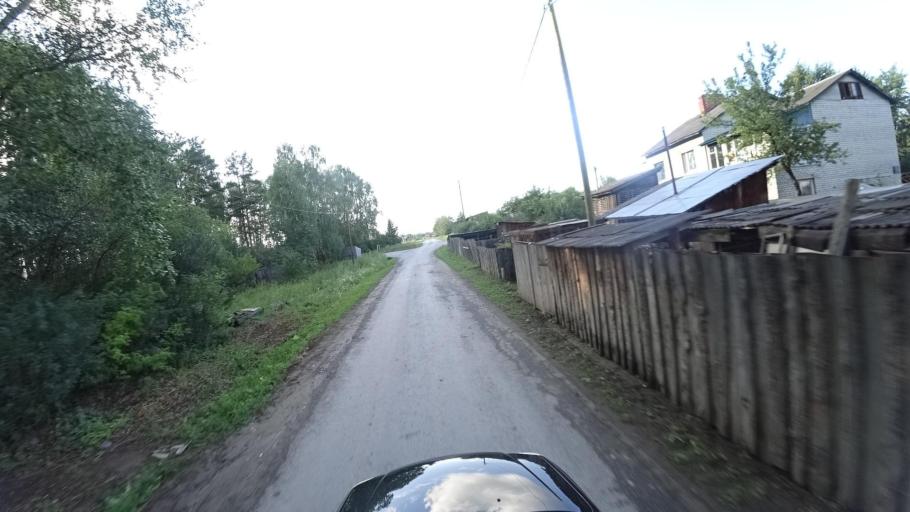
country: RU
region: Sverdlovsk
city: Obukhovskoye
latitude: 56.8485
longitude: 62.6537
